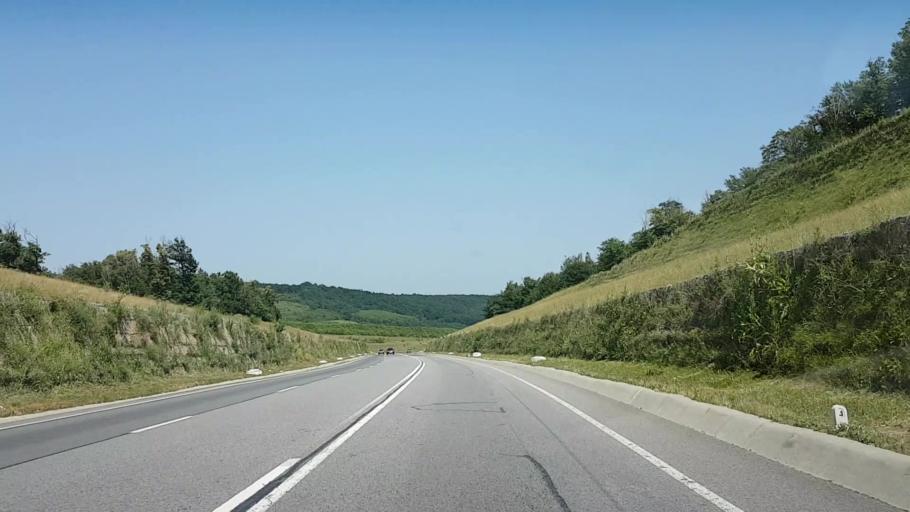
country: RO
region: Cluj
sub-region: Comuna Feleacu
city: Gheorghieni
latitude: 46.7294
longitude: 23.6716
